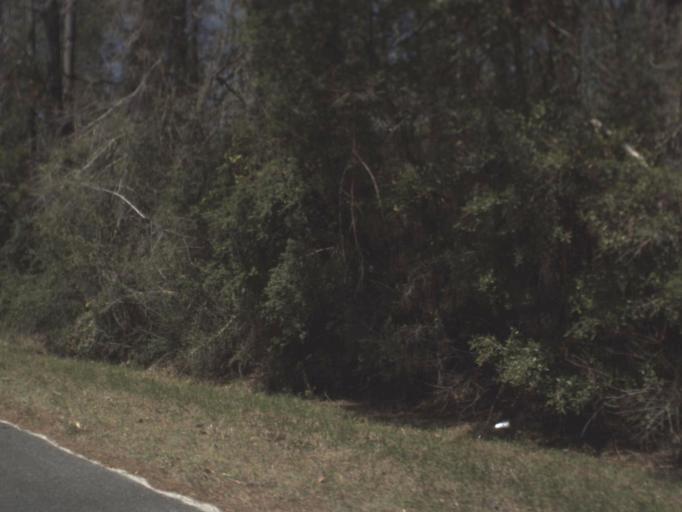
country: US
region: Florida
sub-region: Wakulla County
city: Crawfordville
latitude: 30.2574
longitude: -84.3496
